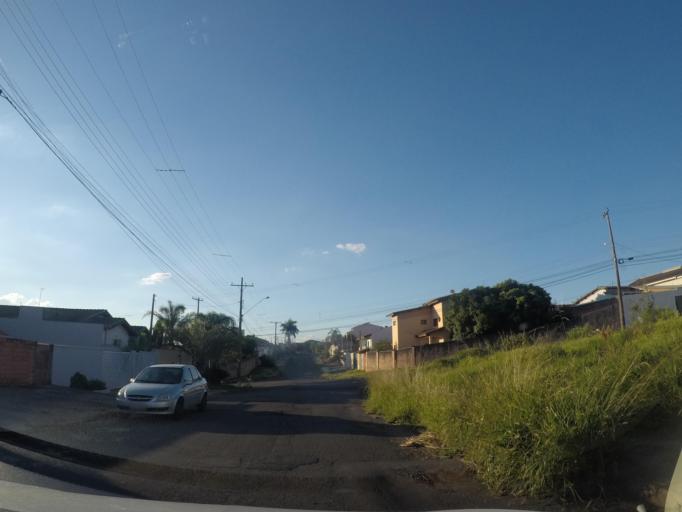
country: BR
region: Sao Paulo
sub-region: Sumare
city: Sumare
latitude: -22.8218
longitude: -47.2526
